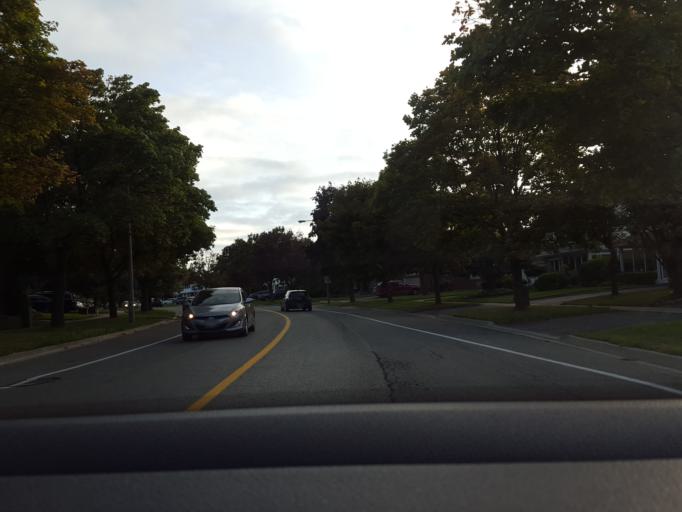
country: CA
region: Ontario
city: Scarborough
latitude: 43.7890
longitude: -79.3072
